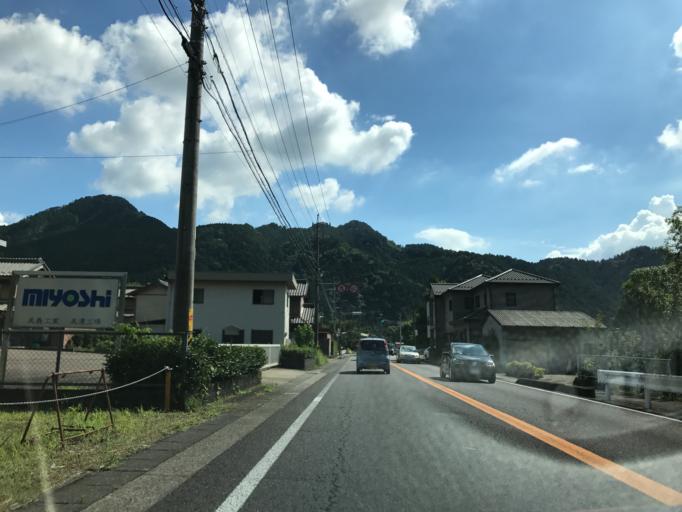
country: JP
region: Gifu
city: Mino
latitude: 35.5727
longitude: 136.9311
